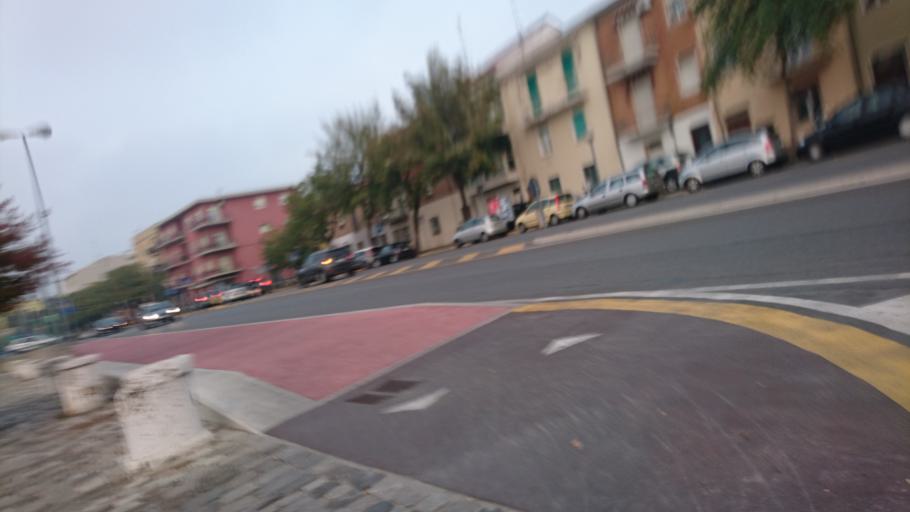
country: IT
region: Emilia-Romagna
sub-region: Provincia di Rimini
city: Rimini
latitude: 44.0669
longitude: 12.5696
